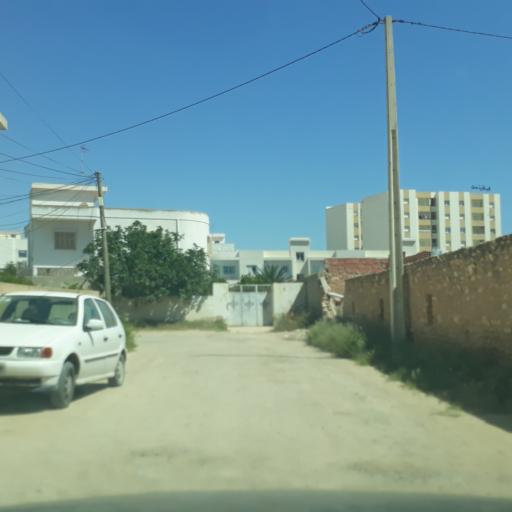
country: TN
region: Safaqis
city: Al Qarmadah
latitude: 34.7987
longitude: 10.7599
